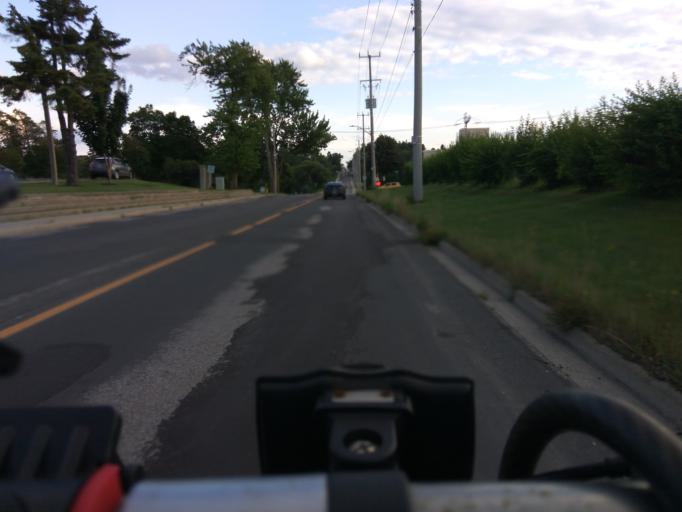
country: CA
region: Ontario
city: Stratford
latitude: 43.3796
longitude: -80.9632
